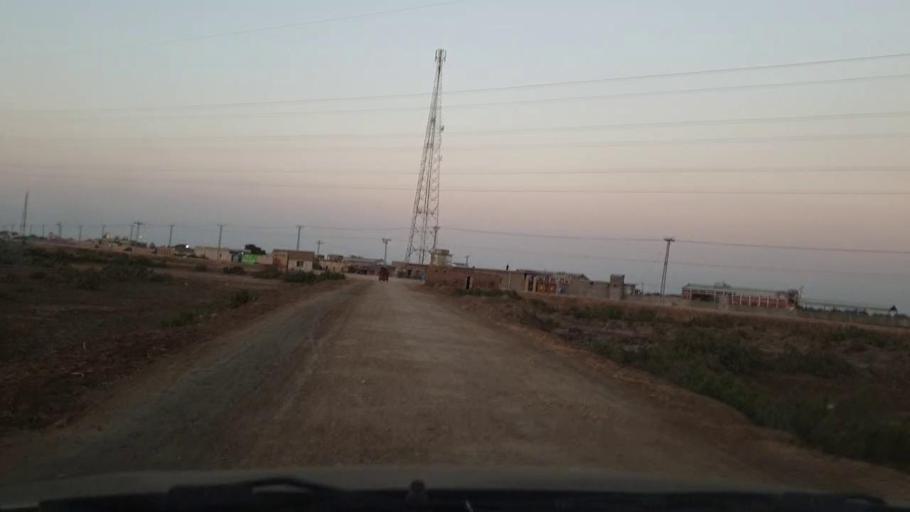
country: PK
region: Sindh
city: Jhol
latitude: 25.9517
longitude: 68.9765
